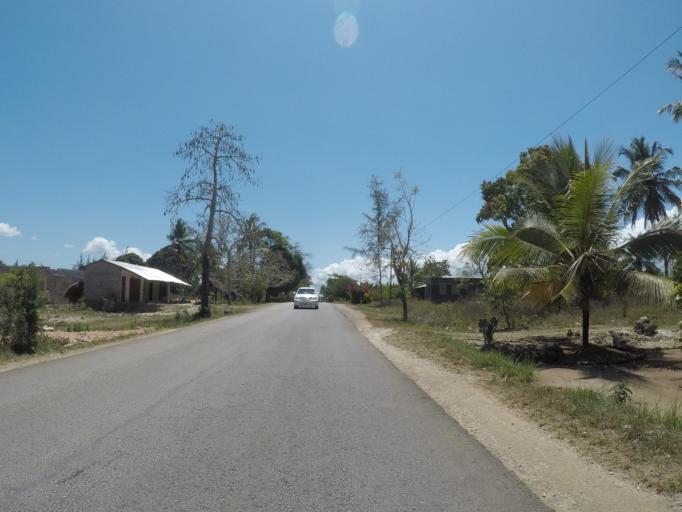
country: TZ
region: Zanzibar Central/South
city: Koani
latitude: -6.2404
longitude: 39.3282
